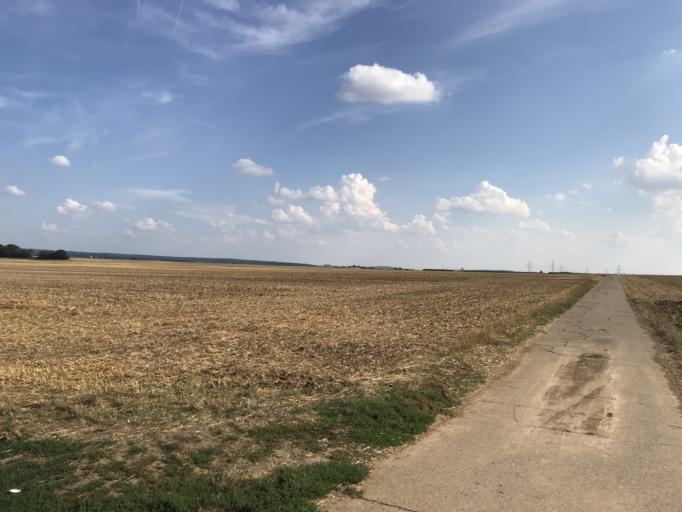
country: DE
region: Hesse
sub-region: Regierungsbezirk Darmstadt
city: Wolfersheim
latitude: 50.3549
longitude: 8.8183
